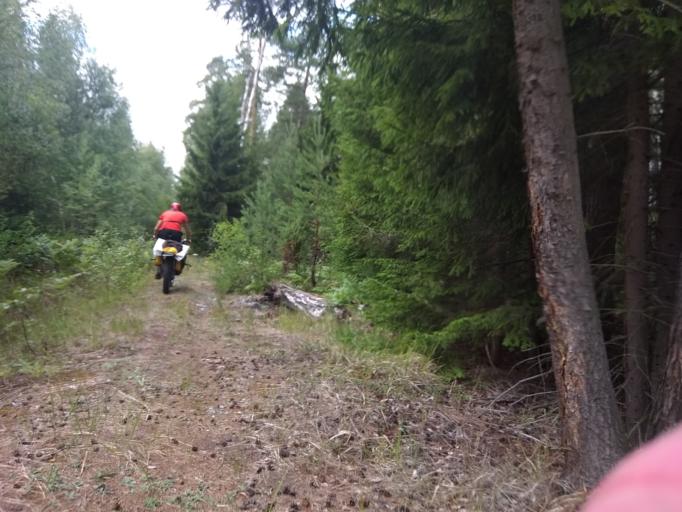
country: RU
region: Moskovskaya
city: Misheronskiy
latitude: 55.6455
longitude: 39.6975
